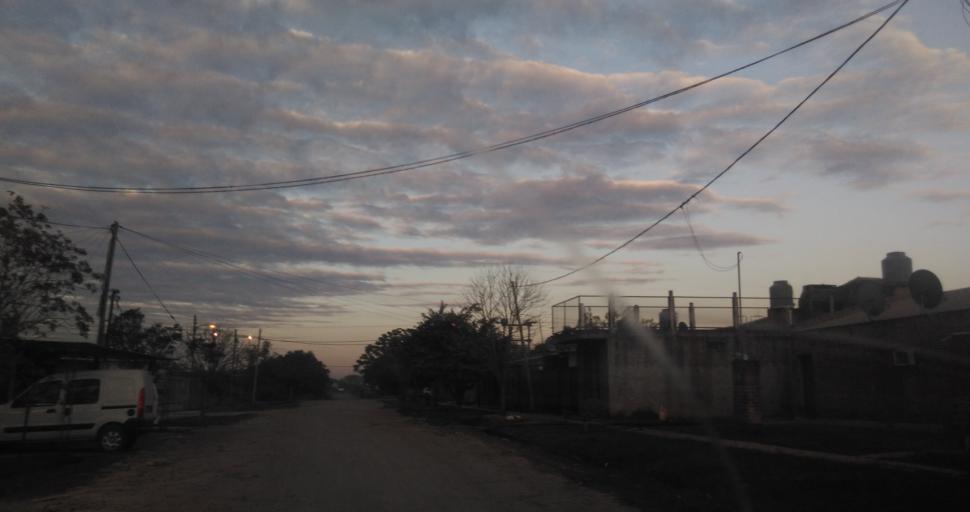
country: AR
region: Chaco
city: Fontana
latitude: -27.4558
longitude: -59.0452
